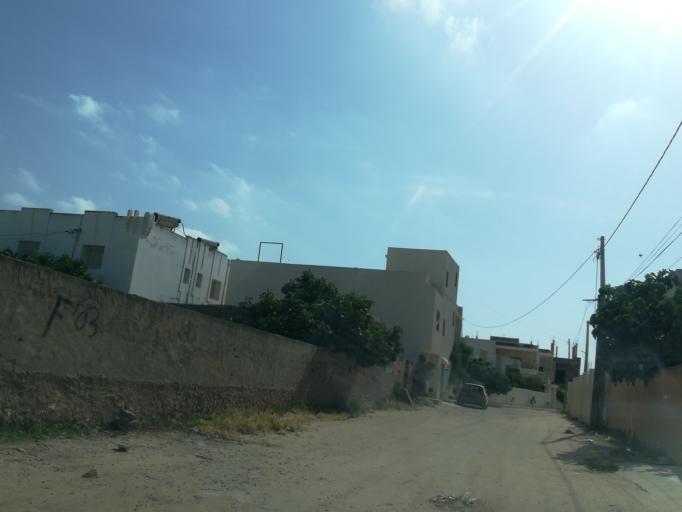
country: TN
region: Safaqis
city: Al Qarmadah
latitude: 34.8151
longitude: 10.7614
